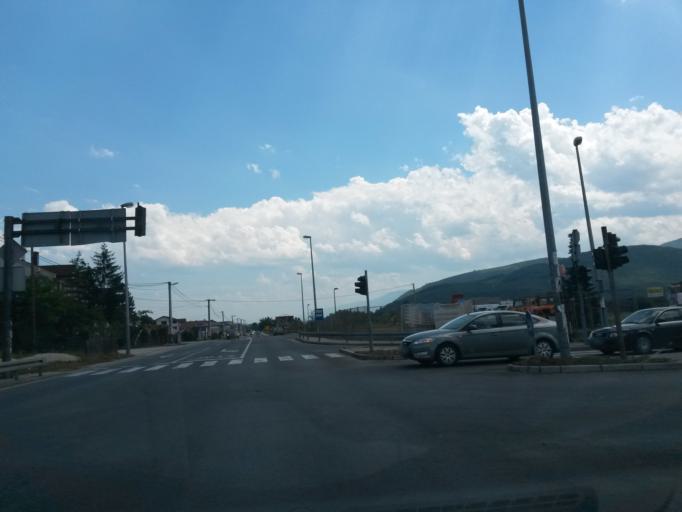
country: BA
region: Federation of Bosnia and Herzegovina
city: Travnik
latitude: 44.2070
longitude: 17.7156
